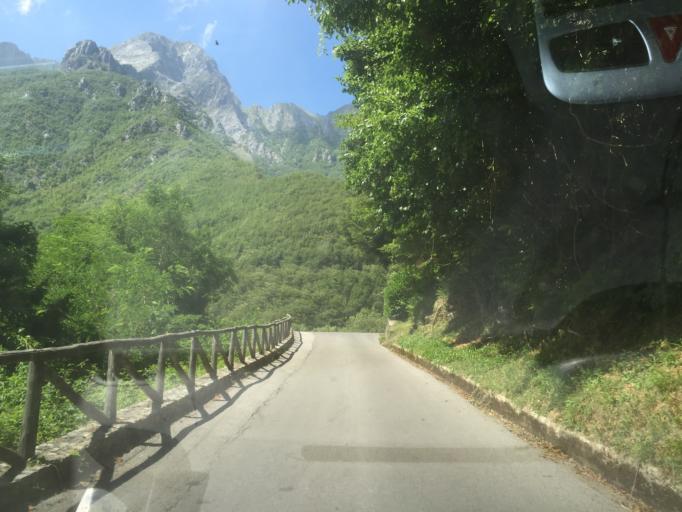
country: IT
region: Tuscany
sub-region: Provincia di Lucca
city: Pontestazzemese
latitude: 44.0266
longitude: 10.3592
